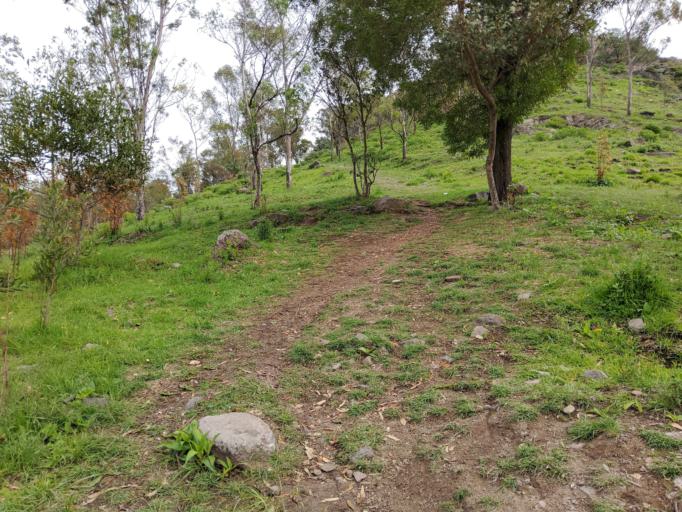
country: MX
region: Mexico
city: Toluca
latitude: 19.3014
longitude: -99.6574
